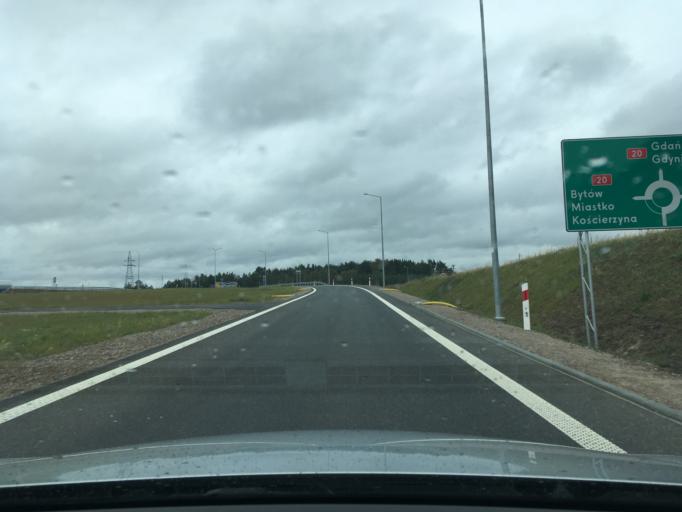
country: PL
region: Pomeranian Voivodeship
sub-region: Powiat koscierski
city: Koscierzyna
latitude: 54.1217
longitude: 18.0190
